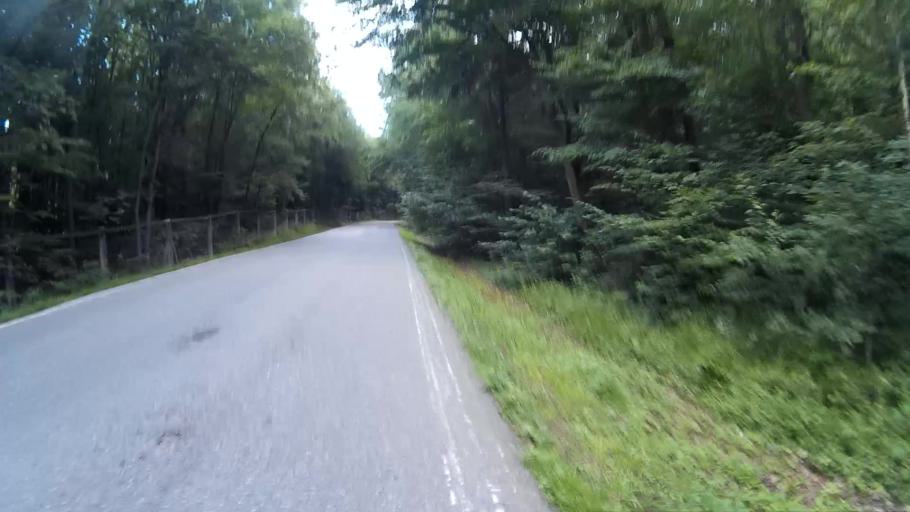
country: CZ
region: South Moravian
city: Ricany
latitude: 49.2076
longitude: 16.4457
